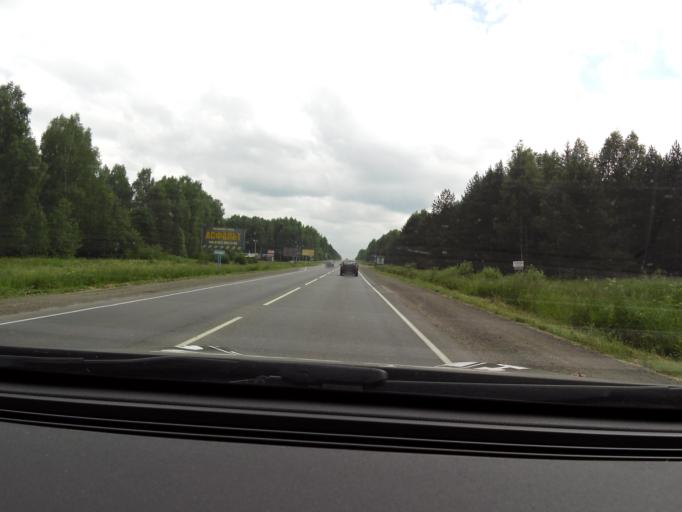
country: RU
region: Perm
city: Kungur
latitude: 57.4149
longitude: 56.8620
